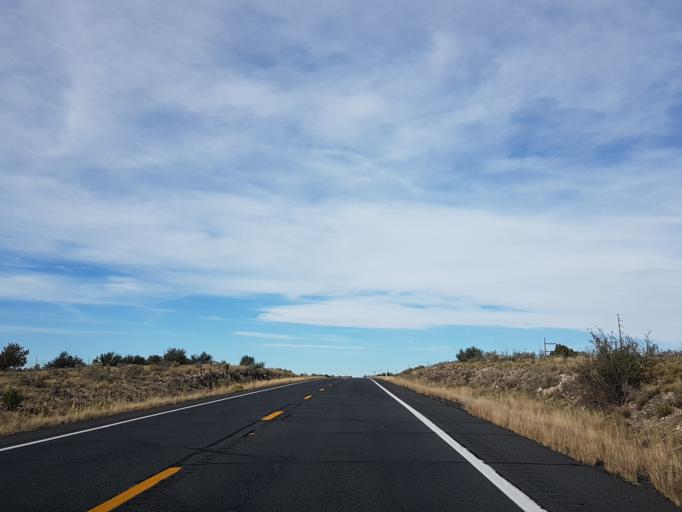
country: US
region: Arizona
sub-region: Coconino County
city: Williams
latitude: 35.5248
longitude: -112.1681
